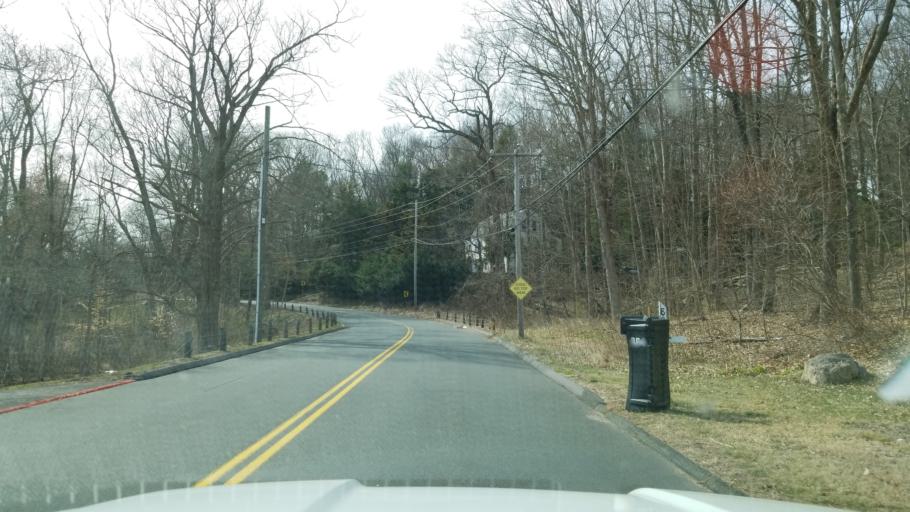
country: US
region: Connecticut
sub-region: Hartford County
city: Glastonbury Center
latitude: 41.6718
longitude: -72.5711
